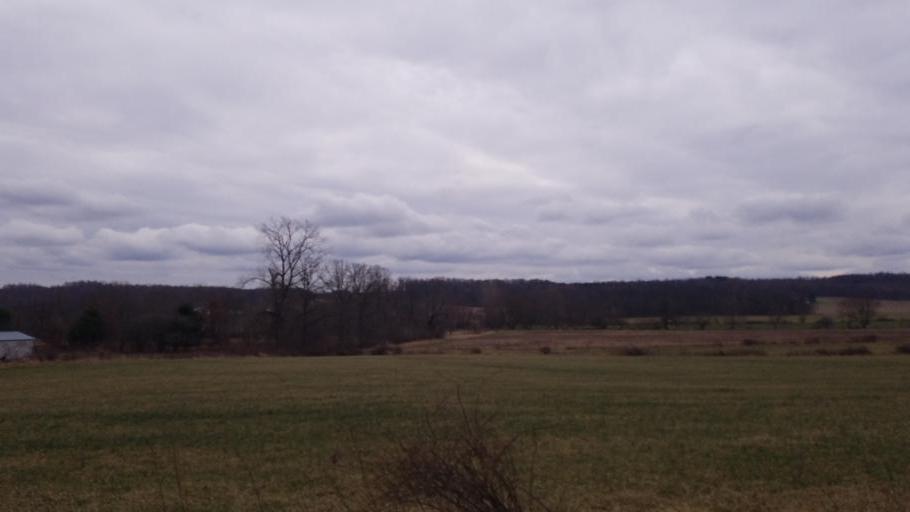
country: US
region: Ohio
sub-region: Sandusky County
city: Bellville
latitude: 40.5987
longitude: -82.5009
